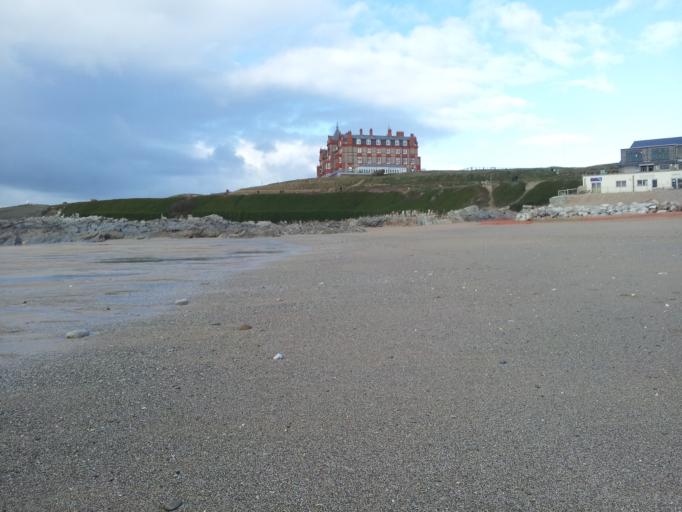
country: GB
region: England
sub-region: Cornwall
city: Newquay
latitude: 50.4185
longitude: -5.0986
